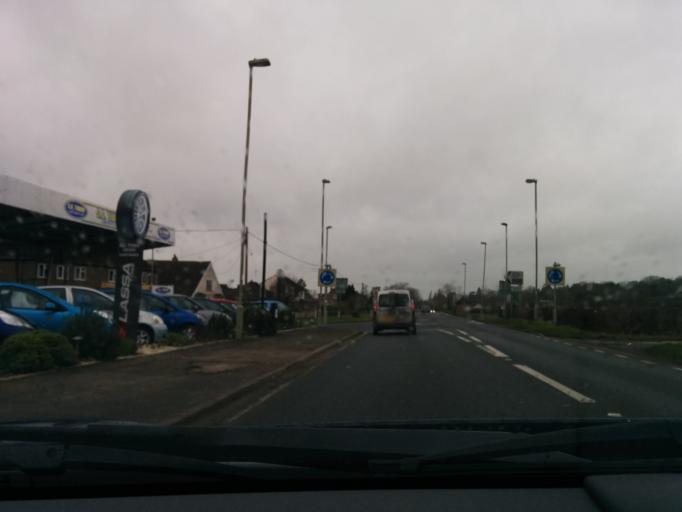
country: GB
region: England
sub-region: Oxfordshire
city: Eynsham
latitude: 51.7602
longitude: -1.3471
